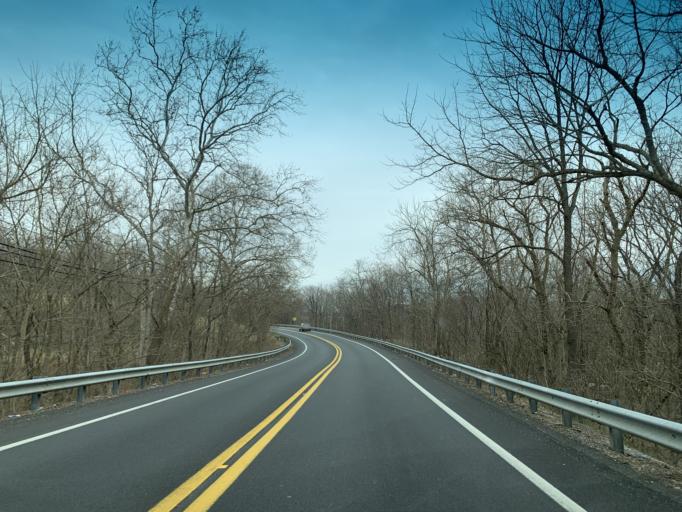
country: US
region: Maryland
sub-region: Washington County
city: Williamsport
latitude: 39.5596
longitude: -77.8899
